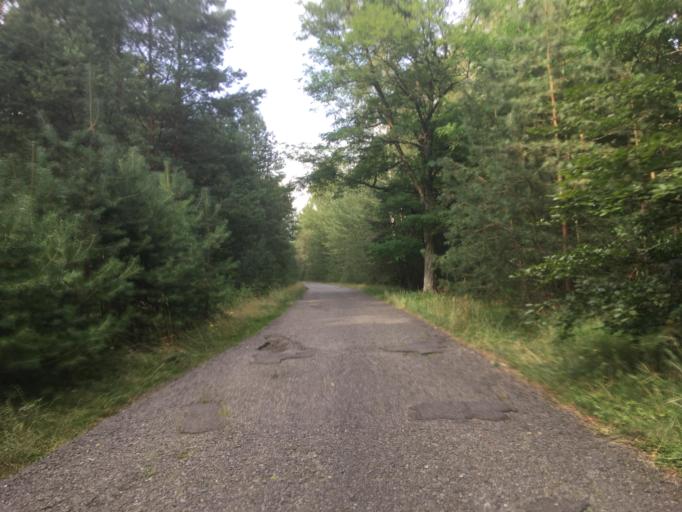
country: DE
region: Brandenburg
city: Melchow
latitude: 52.8067
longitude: 13.7005
